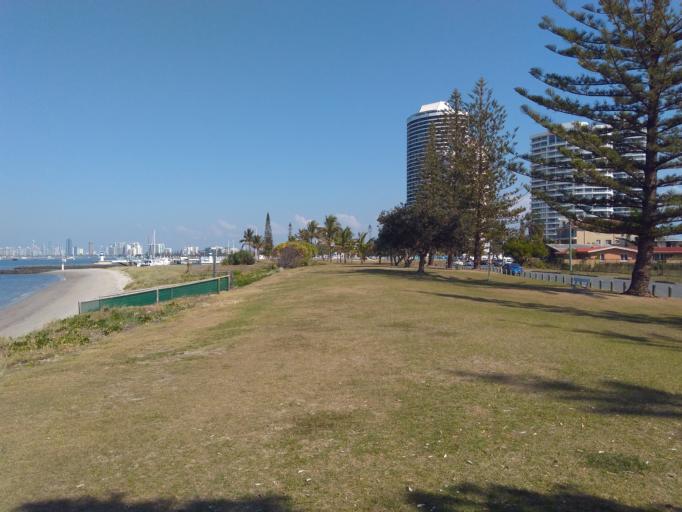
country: AU
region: Queensland
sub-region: Gold Coast
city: Southport
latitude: -27.9211
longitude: 153.4070
